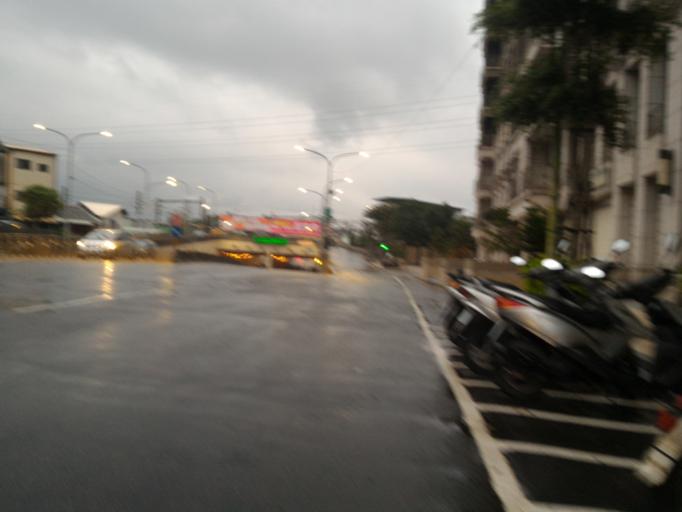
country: TW
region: Taipei
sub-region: Taipei
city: Banqiao
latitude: 24.9830
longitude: 121.4113
